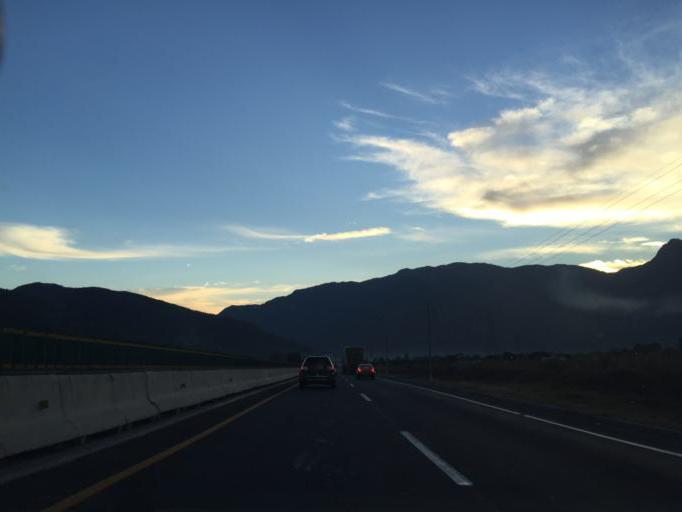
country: MX
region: Veracruz
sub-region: Nogales
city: Agricola Lazaro Cardenas
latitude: 18.8154
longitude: -97.2107
